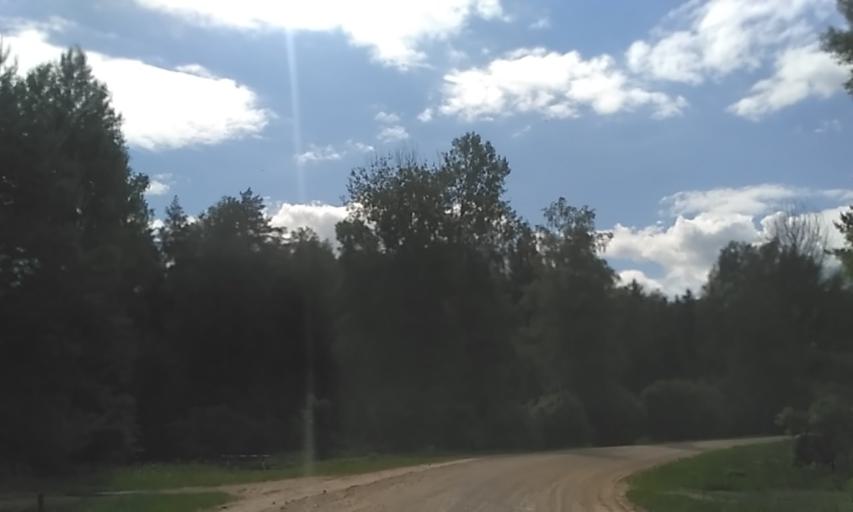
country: BY
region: Minsk
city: Khalopyenichy
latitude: 54.5144
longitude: 29.0643
